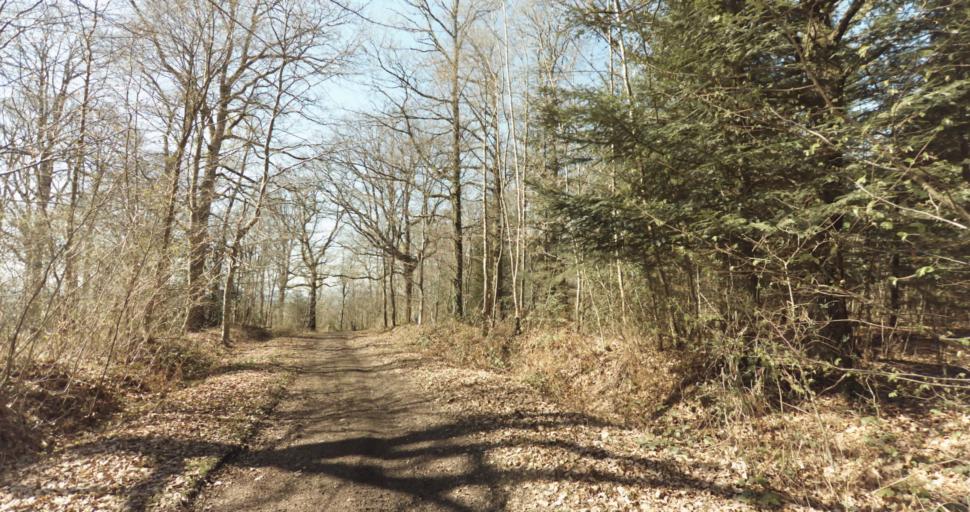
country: FR
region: Lower Normandy
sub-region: Departement du Calvados
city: Saint-Pierre-sur-Dives
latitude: 49.0034
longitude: 0.0469
